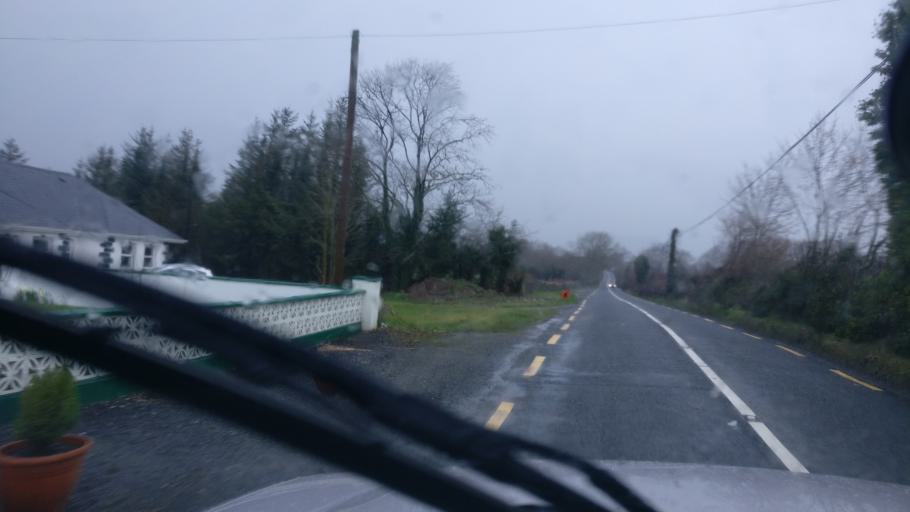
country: IE
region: Connaught
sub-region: County Galway
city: Loughrea
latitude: 53.1541
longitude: -8.4791
